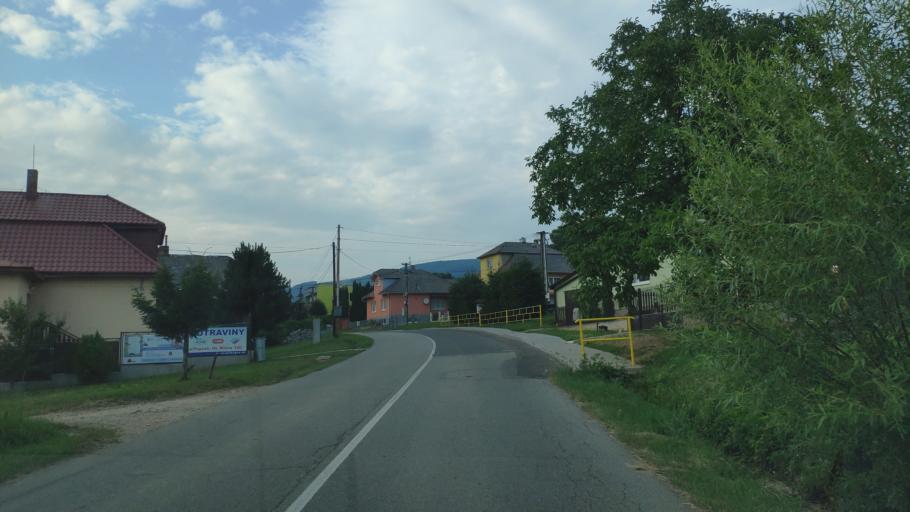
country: SK
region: Kosicky
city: Medzev
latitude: 48.7037
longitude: 20.9749
